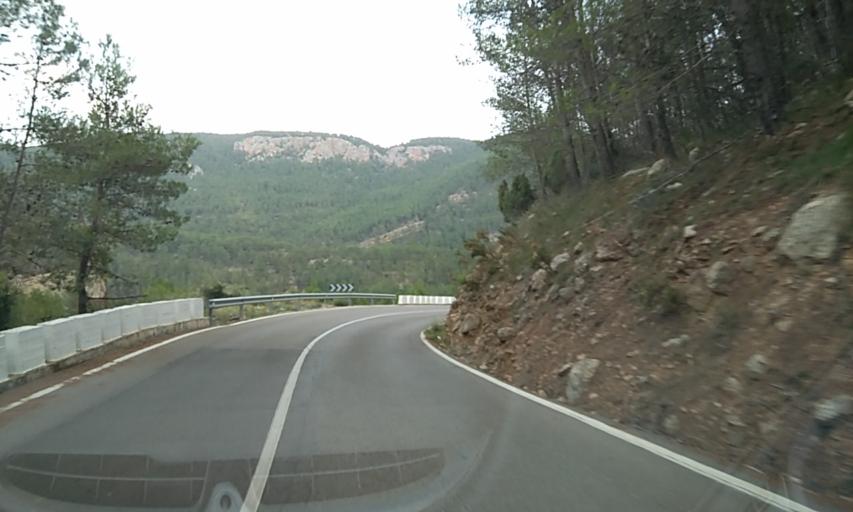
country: ES
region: Valencia
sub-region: Provincia de Castello
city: Montanejos
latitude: 40.0830
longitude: -0.5476
